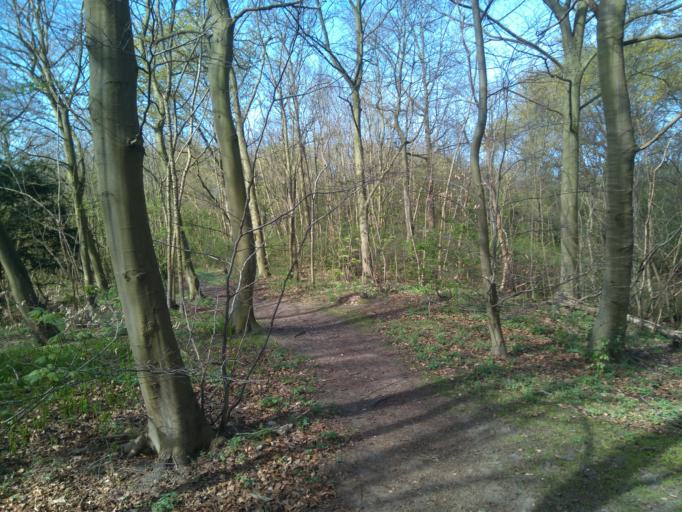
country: NL
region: South Holland
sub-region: Gemeente Den Haag
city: The Hague
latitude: 52.0948
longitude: 4.2976
